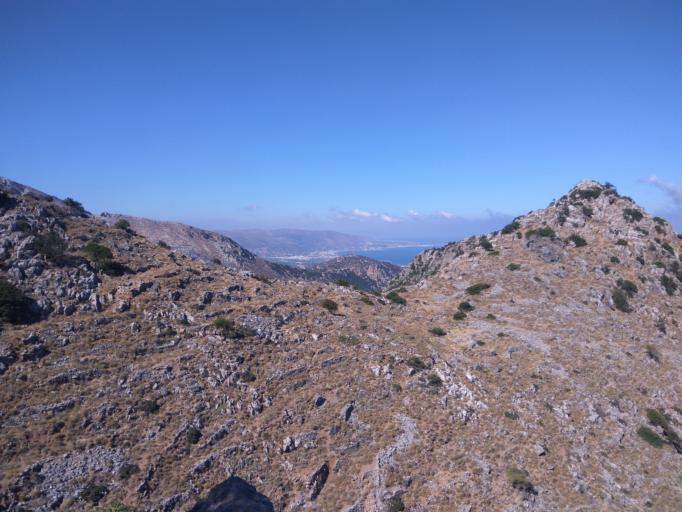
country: GR
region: Crete
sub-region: Nomos Lasithiou
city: Paralia Milatou
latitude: 35.2801
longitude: 25.5638
